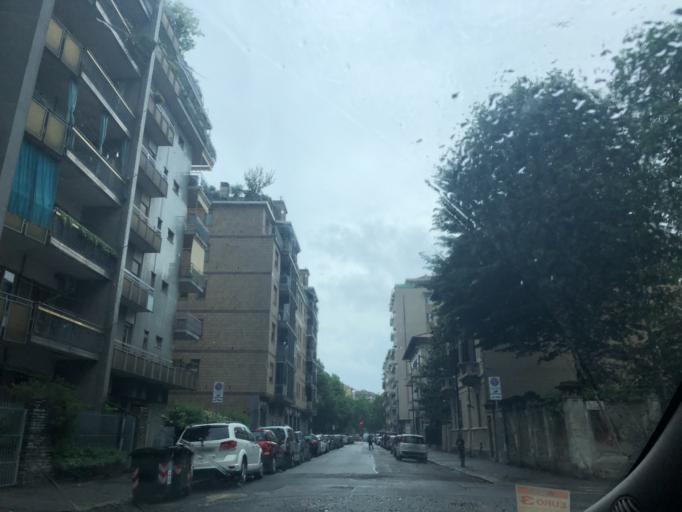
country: IT
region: Piedmont
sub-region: Provincia di Torino
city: Lesna
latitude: 45.0774
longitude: 7.6360
